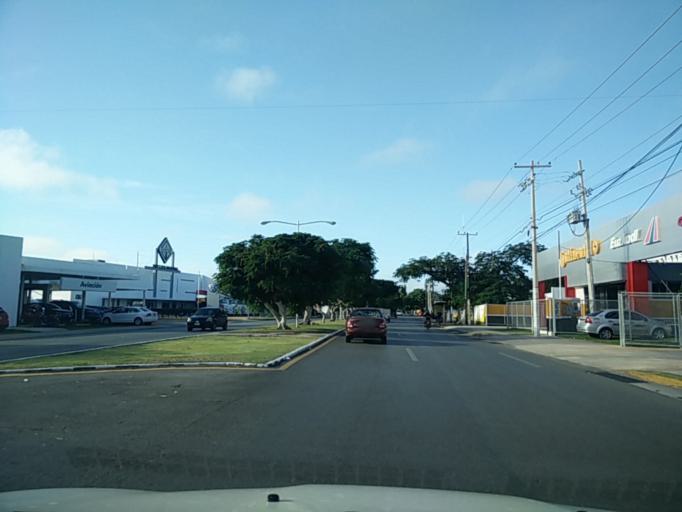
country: MX
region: Yucatan
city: Merida
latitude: 20.9539
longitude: -89.6444
